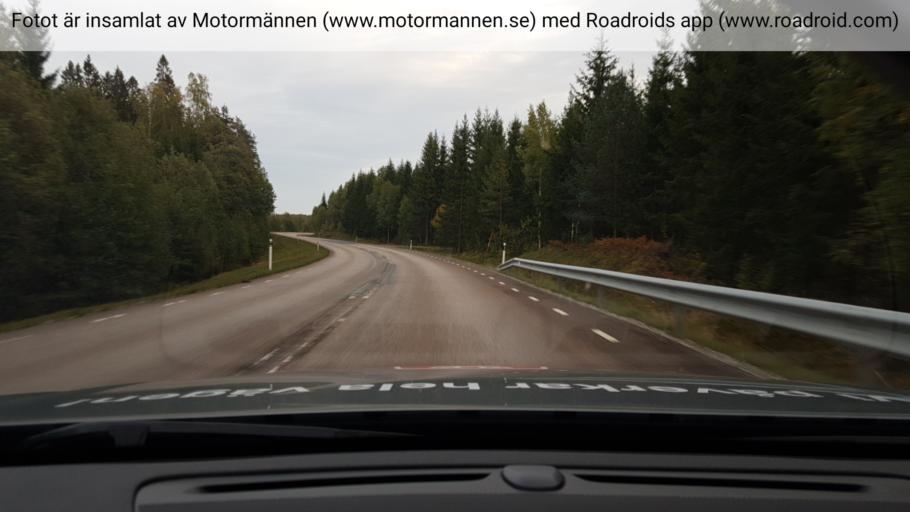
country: SE
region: Vaestra Goetaland
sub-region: Amals Kommun
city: Amal
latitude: 59.0782
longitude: 12.6263
